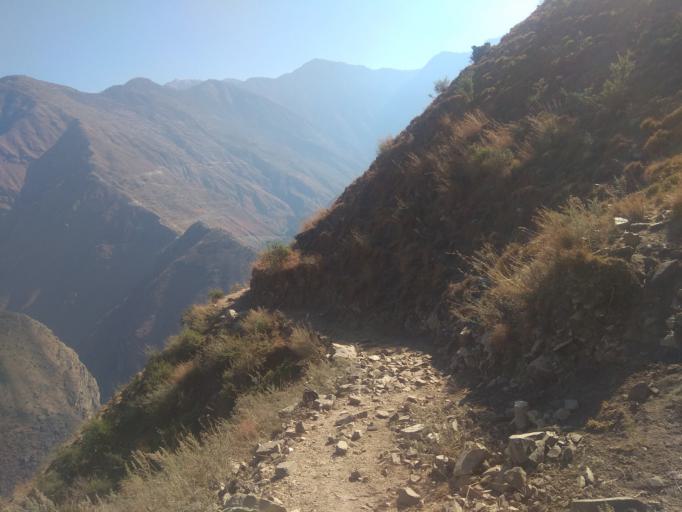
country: NP
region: Mid Western
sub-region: Karnali Zone
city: Jumla
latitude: 29.3150
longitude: 81.7448
